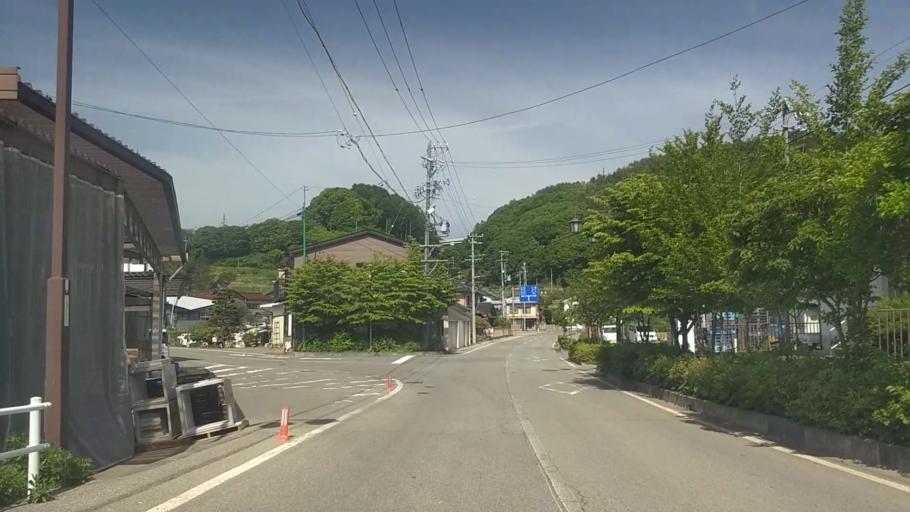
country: JP
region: Nagano
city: Saku
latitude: 36.1316
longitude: 138.4728
